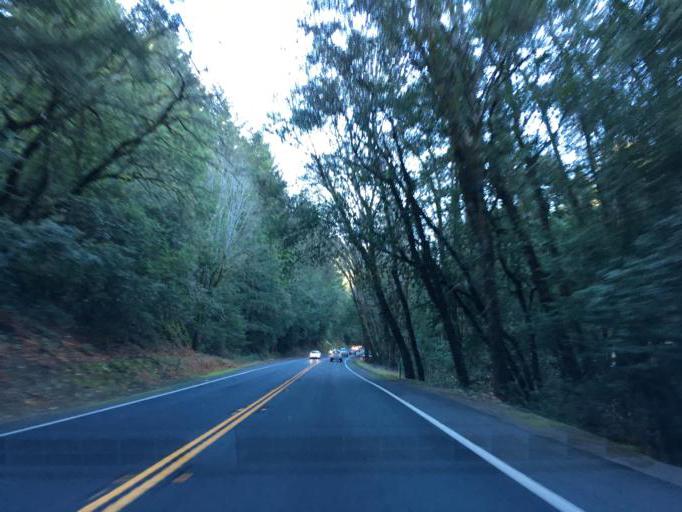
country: US
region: California
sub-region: Mendocino County
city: Brooktrails
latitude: 39.4978
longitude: -123.3701
